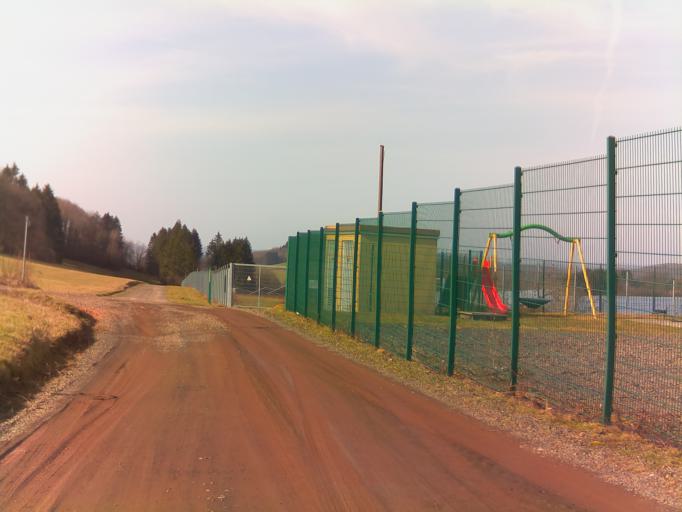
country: DE
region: Saarland
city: Freisen
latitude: 49.5228
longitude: 7.2237
